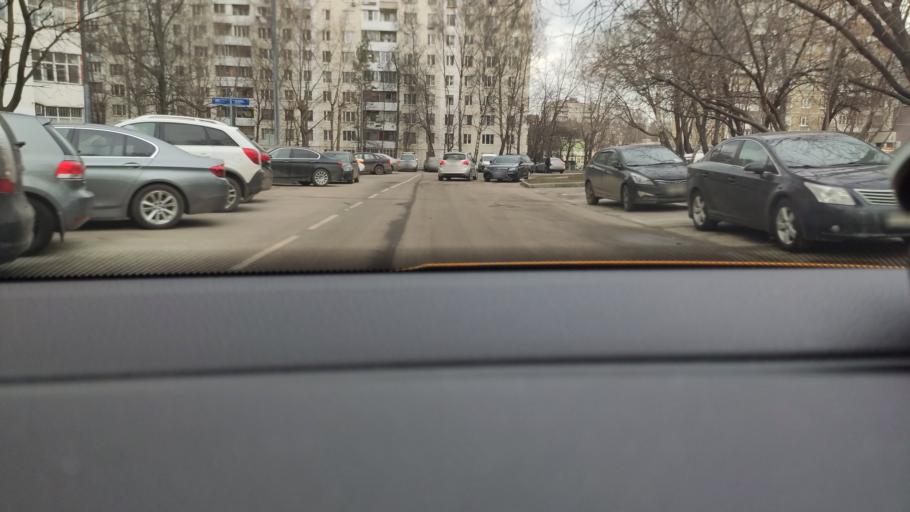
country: RU
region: Moscow
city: Altuf'yevskiy
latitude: 55.8771
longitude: 37.5768
